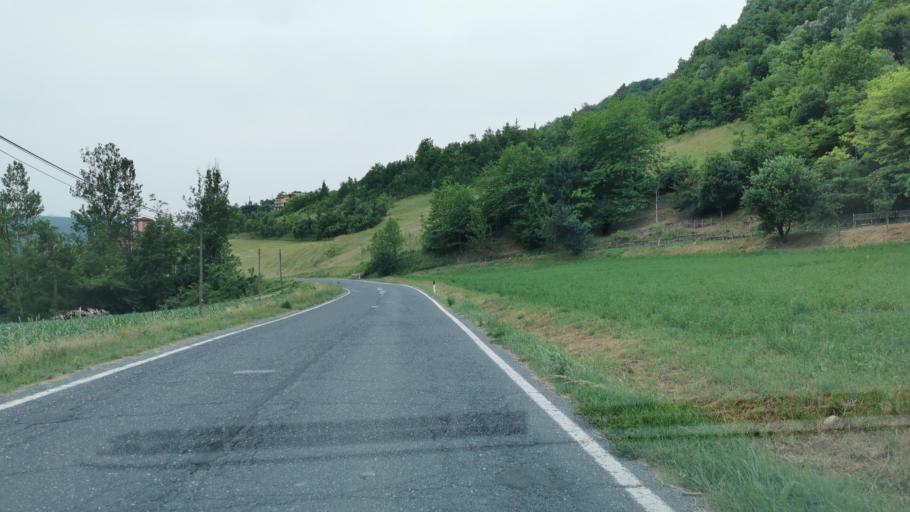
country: IT
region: Piedmont
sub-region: Provincia di Cuneo
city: Ceva
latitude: 44.3929
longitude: 8.0460
